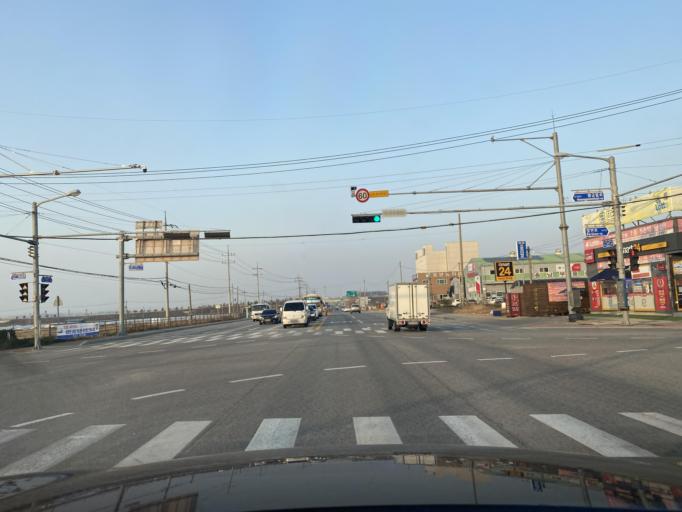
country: KR
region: Chungcheongnam-do
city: Yesan
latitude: 36.6986
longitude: 126.8290
